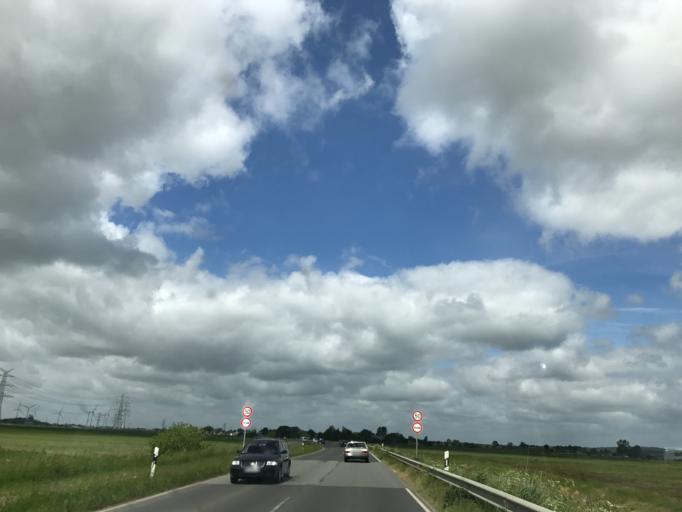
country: DE
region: Schleswig-Holstein
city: Eddelak
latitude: 53.9335
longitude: 9.1500
